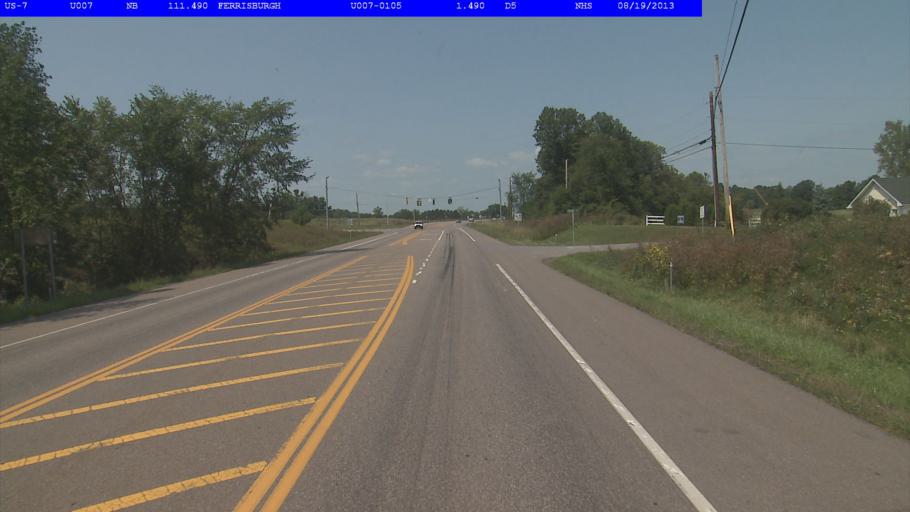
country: US
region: Vermont
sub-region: Addison County
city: Vergennes
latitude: 44.1833
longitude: -73.2395
